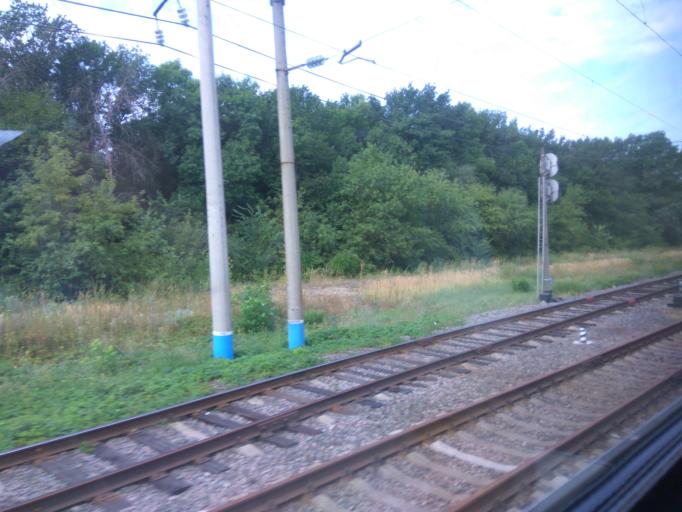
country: RU
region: Saratov
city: Rtishchevo
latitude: 52.2048
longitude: 43.8908
